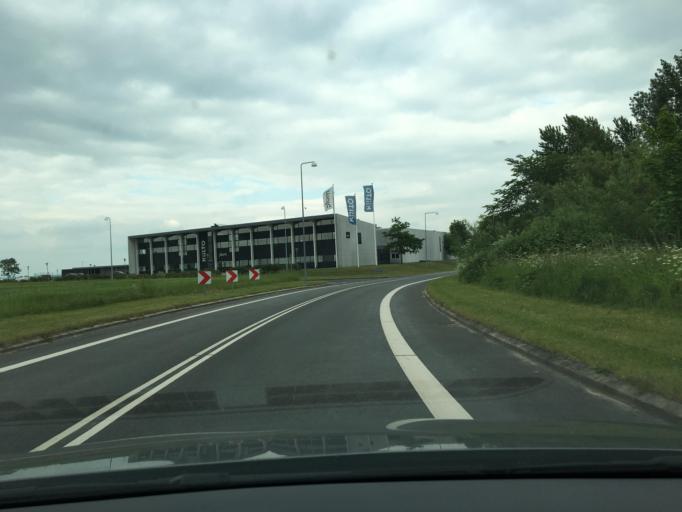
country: DK
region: South Denmark
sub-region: Assens Kommune
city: Assens
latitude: 55.2820
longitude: 9.9163
